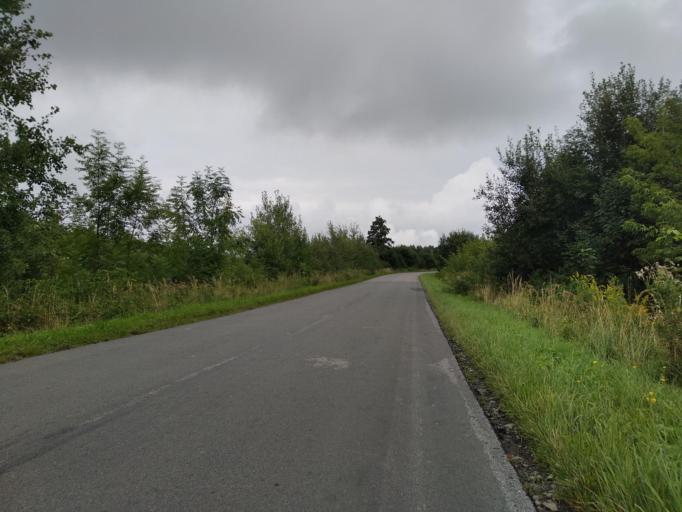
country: PL
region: Subcarpathian Voivodeship
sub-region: Powiat rzeszowski
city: Dynow
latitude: 49.7223
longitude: 22.3132
